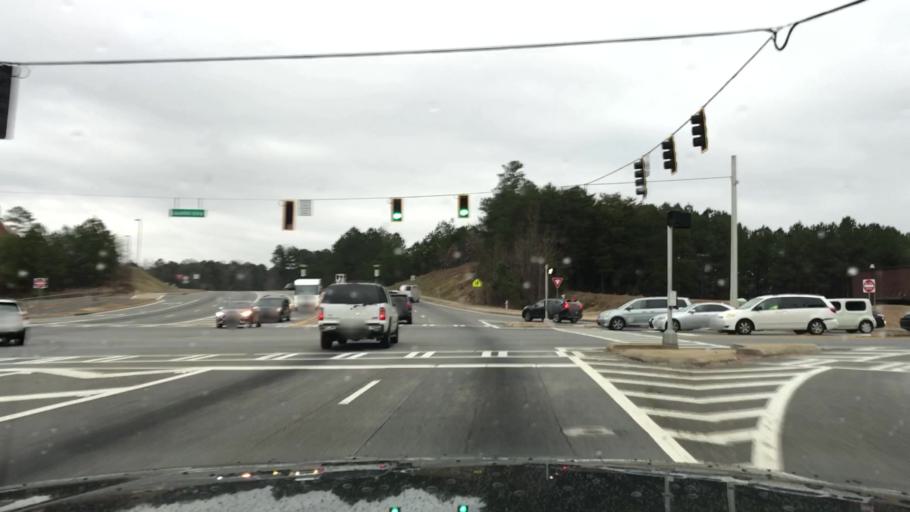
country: US
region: Georgia
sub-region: Gwinnett County
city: Suwanee
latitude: 34.0317
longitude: -84.0669
